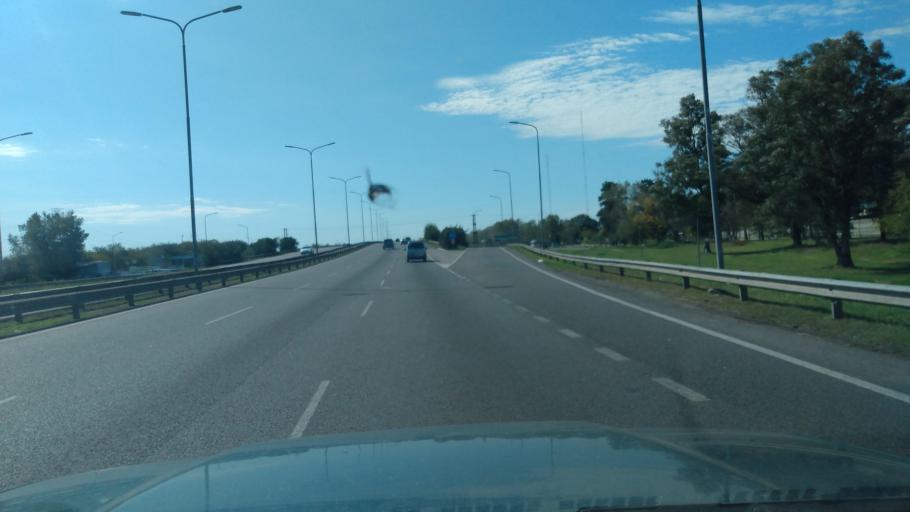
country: AR
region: Buenos Aires
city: Hurlingham
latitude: -34.5863
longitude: -58.6796
